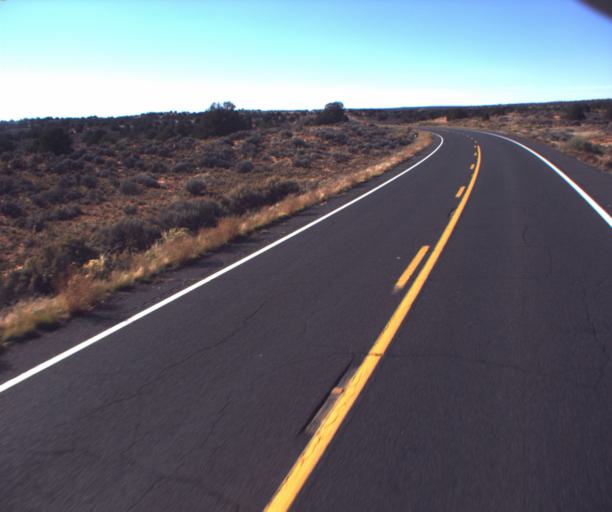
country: US
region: Arizona
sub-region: Coconino County
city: Kaibito
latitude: 36.5762
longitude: -110.7721
